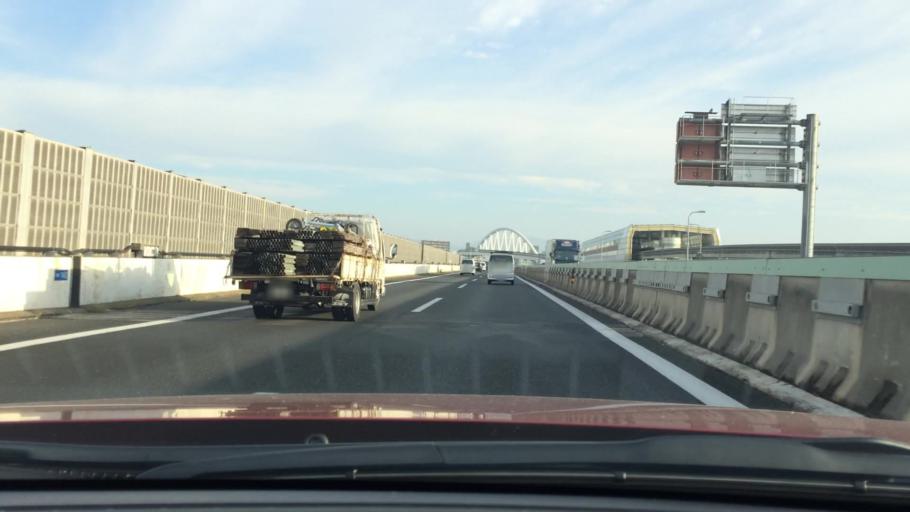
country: JP
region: Osaka
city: Ibaraki
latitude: 34.7912
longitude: 135.5647
